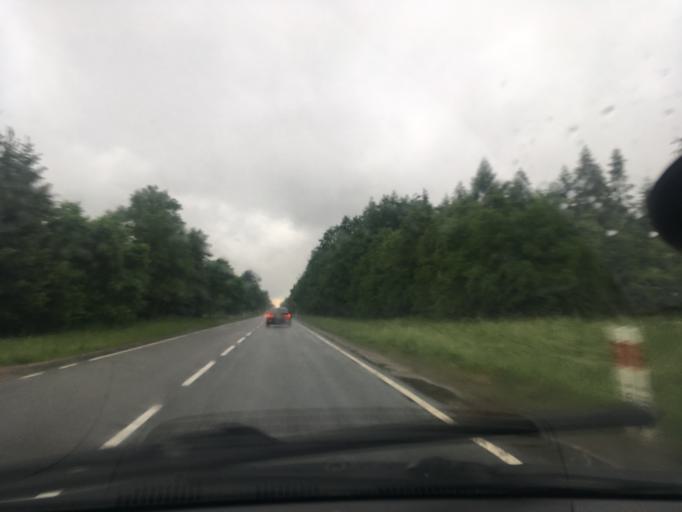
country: PL
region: Lublin Voivodeship
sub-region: Powiat rycki
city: Ryki
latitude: 51.5873
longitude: 21.9322
